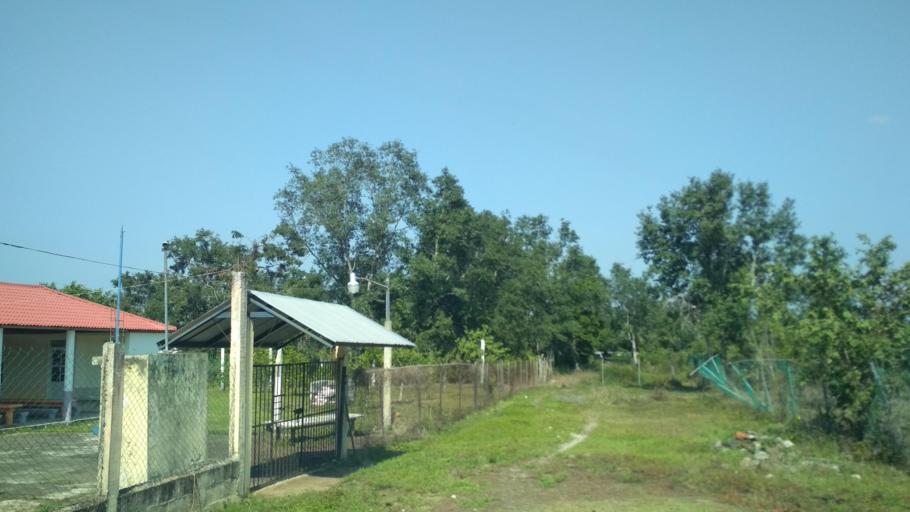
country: MX
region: Puebla
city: San Jose Acateno
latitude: 20.1768
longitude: -97.2316
